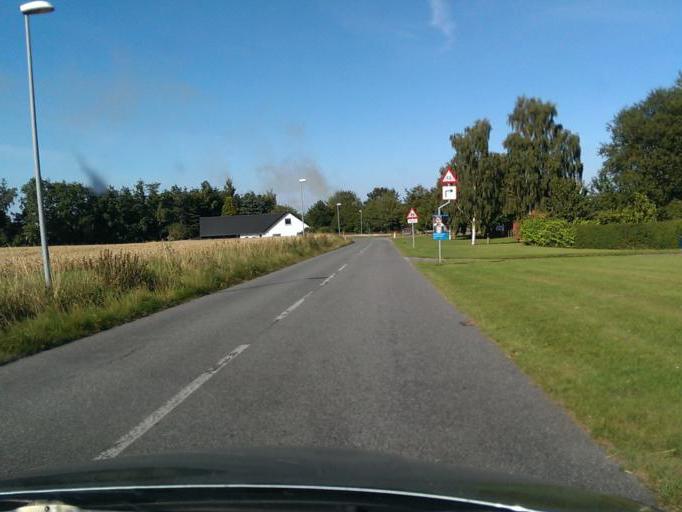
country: DK
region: Central Jutland
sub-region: Odder Kommune
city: Odder
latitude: 55.9134
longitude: 10.1398
